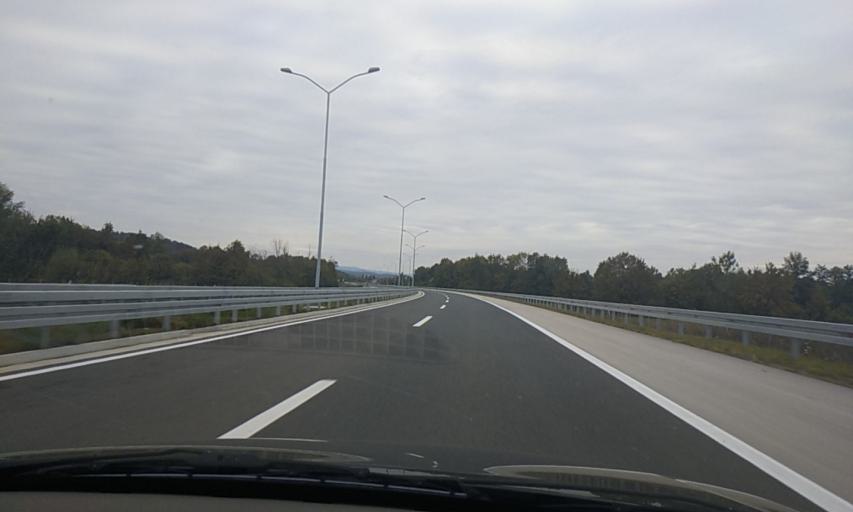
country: BA
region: Republika Srpska
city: Maglajani
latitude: 44.8959
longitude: 17.3636
